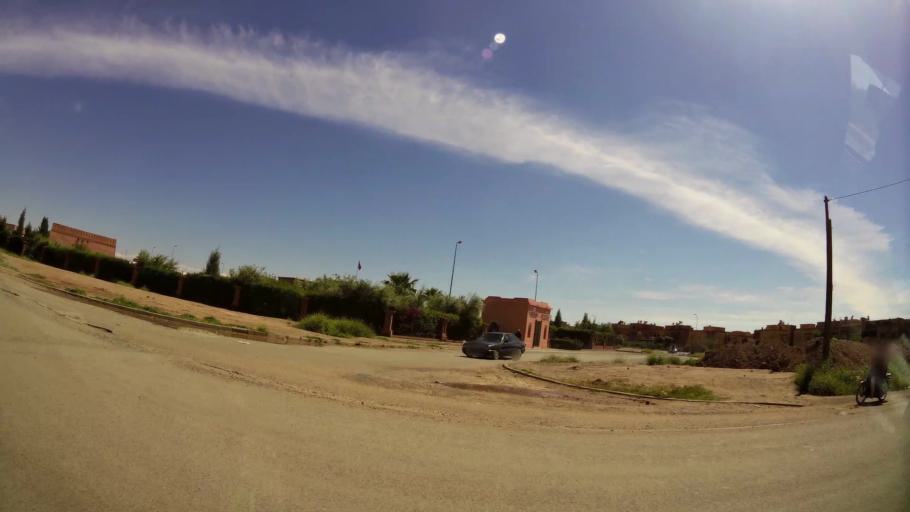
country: MA
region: Marrakech-Tensift-Al Haouz
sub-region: Marrakech
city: Marrakesh
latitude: 31.6407
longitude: -8.1044
